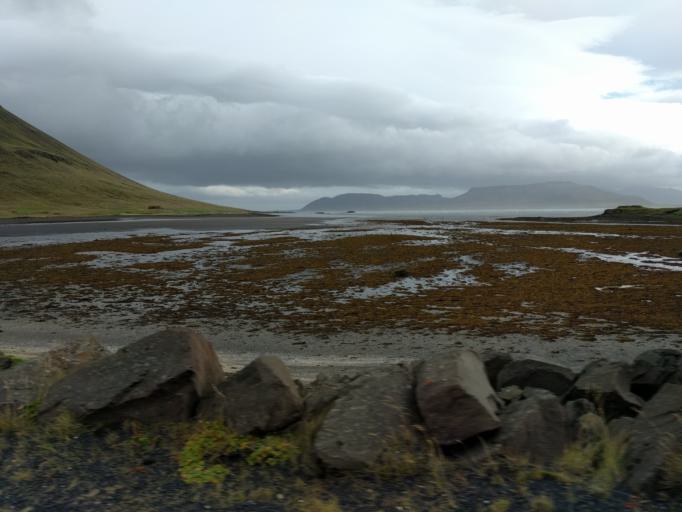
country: IS
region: West
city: Olafsvik
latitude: 64.9266
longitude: -23.3044
